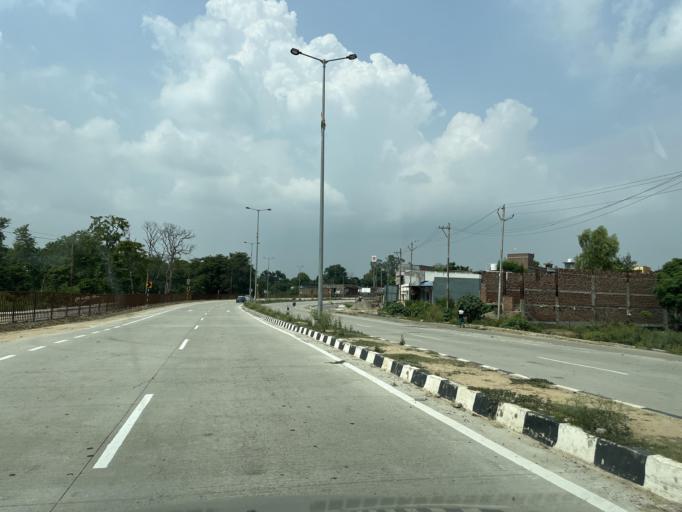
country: IN
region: Uttar Pradesh
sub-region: Bijnor
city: Sherkot
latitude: 29.3314
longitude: 78.5679
